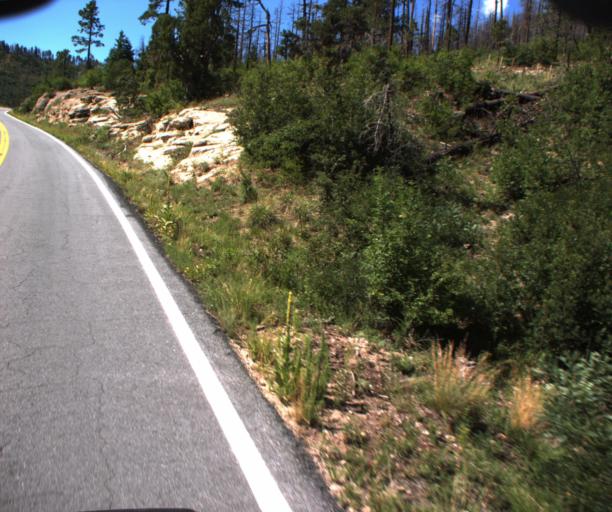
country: US
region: Arizona
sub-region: Apache County
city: Eagar
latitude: 33.8222
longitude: -109.1549
